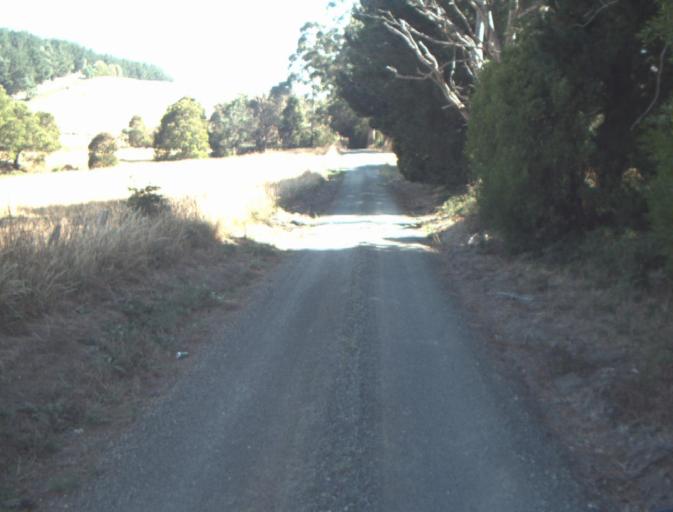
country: AU
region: Tasmania
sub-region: Launceston
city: Mayfield
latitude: -41.1718
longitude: 147.2127
